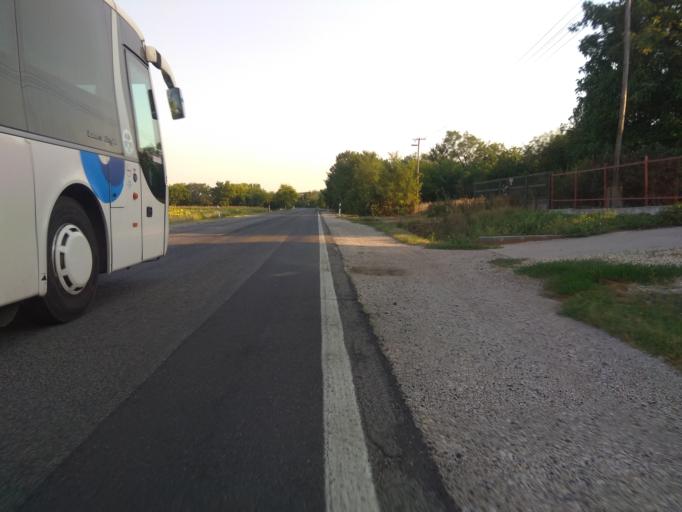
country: HU
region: Borsod-Abauj-Zemplen
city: Nyekladhaza
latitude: 47.9768
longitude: 20.8302
